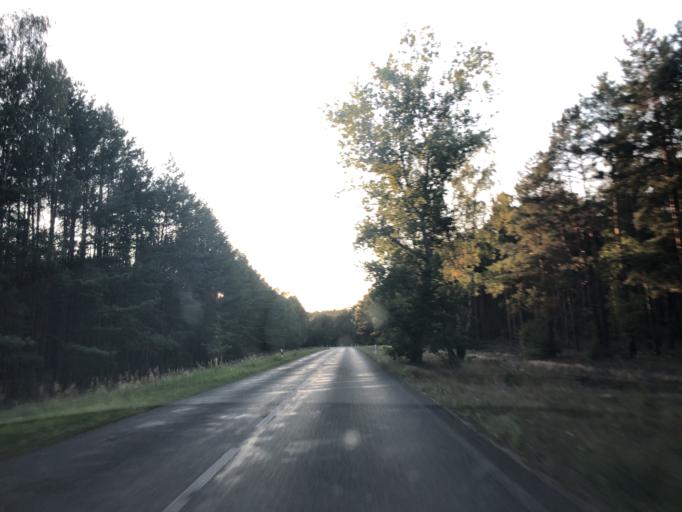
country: DE
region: Brandenburg
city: Mullrose
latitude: 52.2477
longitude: 14.4675
